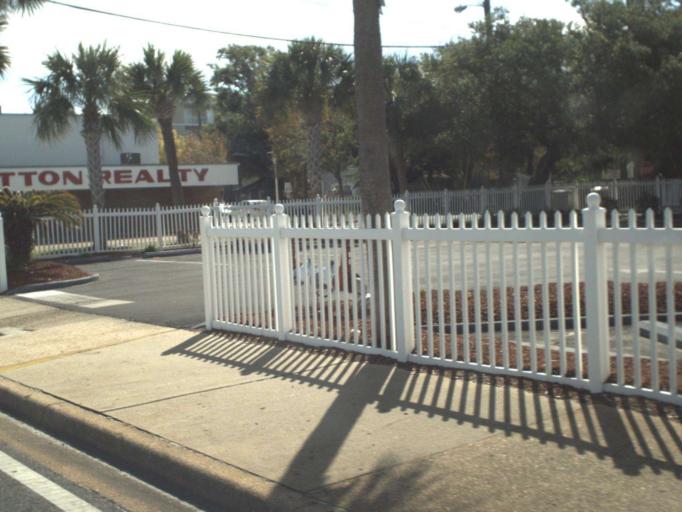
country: US
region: Florida
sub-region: Okaloosa County
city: Fort Walton Beach
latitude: 30.4038
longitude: -86.6097
